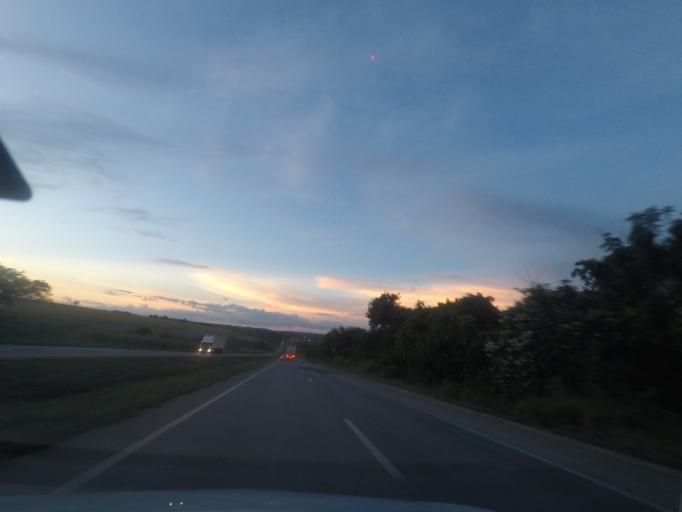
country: BR
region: Goias
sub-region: Morrinhos
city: Morrinhos
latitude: -17.5401
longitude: -49.2108
